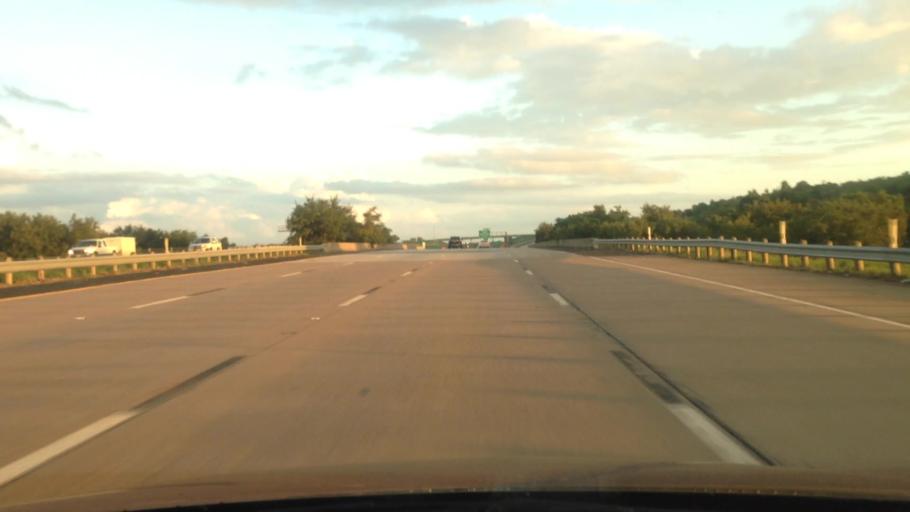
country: US
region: Texas
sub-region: Tarrant County
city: Benbrook
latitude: 32.7128
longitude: -97.4778
